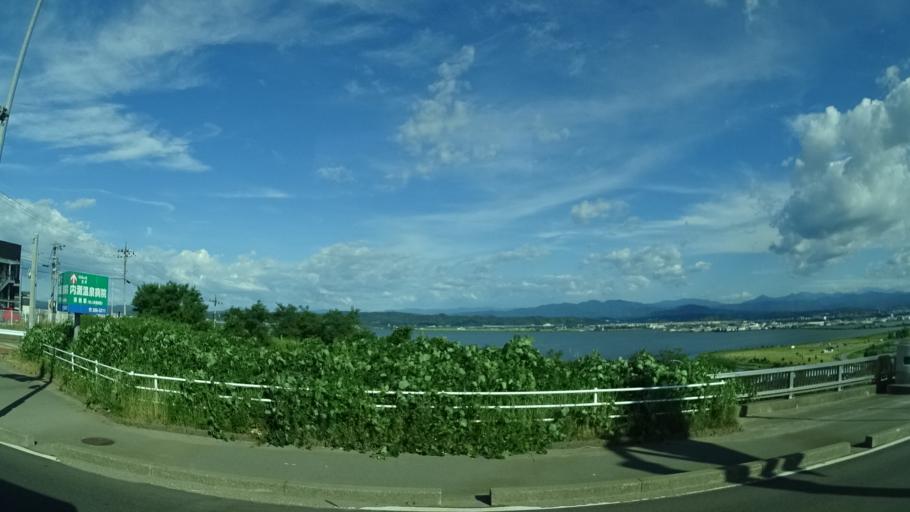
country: JP
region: Ishikawa
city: Kanazawa-shi
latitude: 36.6618
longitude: 136.6521
